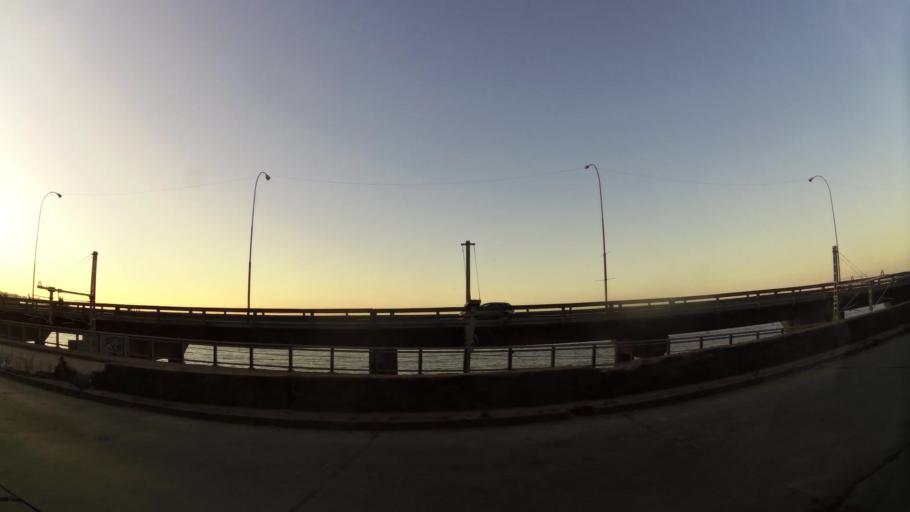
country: CL
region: Valparaiso
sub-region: Provincia de Valparaiso
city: Vina del Mar
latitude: -33.0256
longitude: -71.5728
